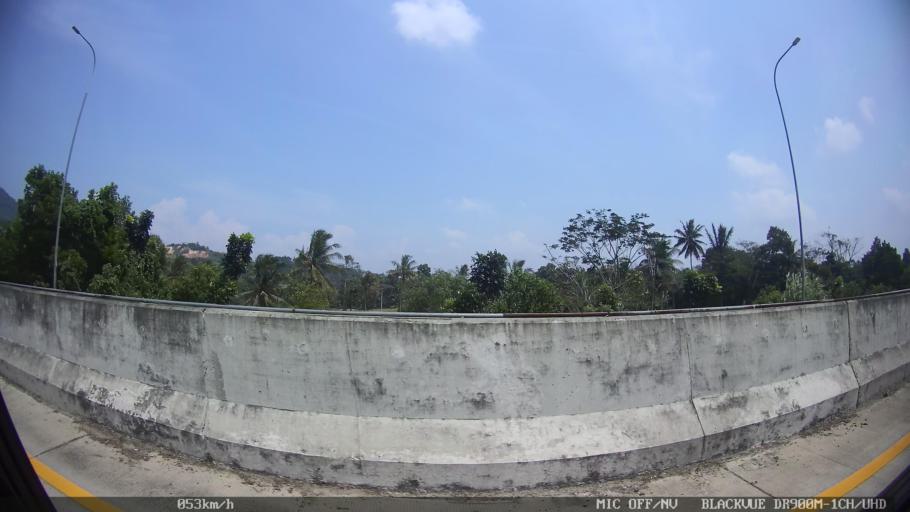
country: ID
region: Lampung
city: Panjang
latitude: -5.3973
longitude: 105.3483
